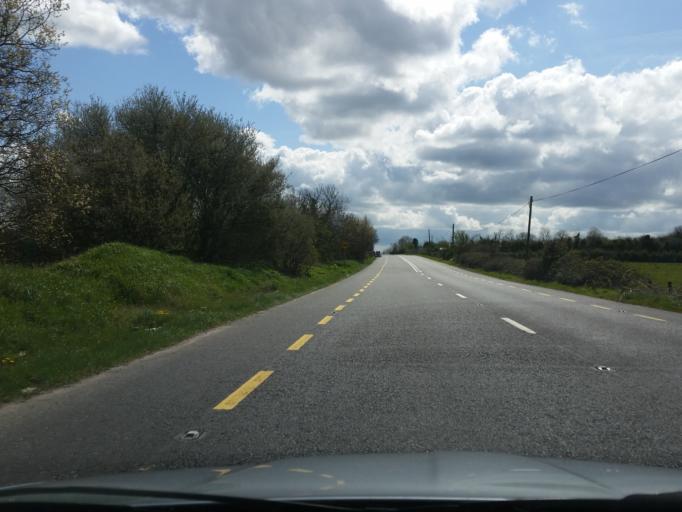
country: IE
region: Leinster
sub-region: An Mhi
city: Slane
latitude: 53.6799
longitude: -6.5392
